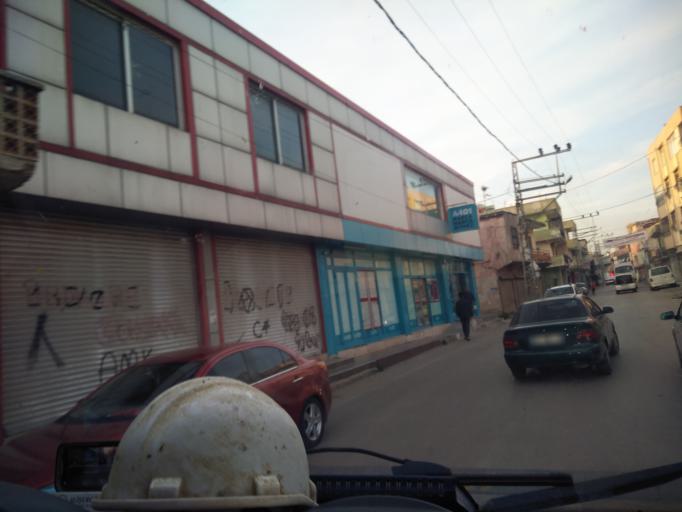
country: TR
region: Adana
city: Seyhan
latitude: 36.9994
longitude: 35.2799
